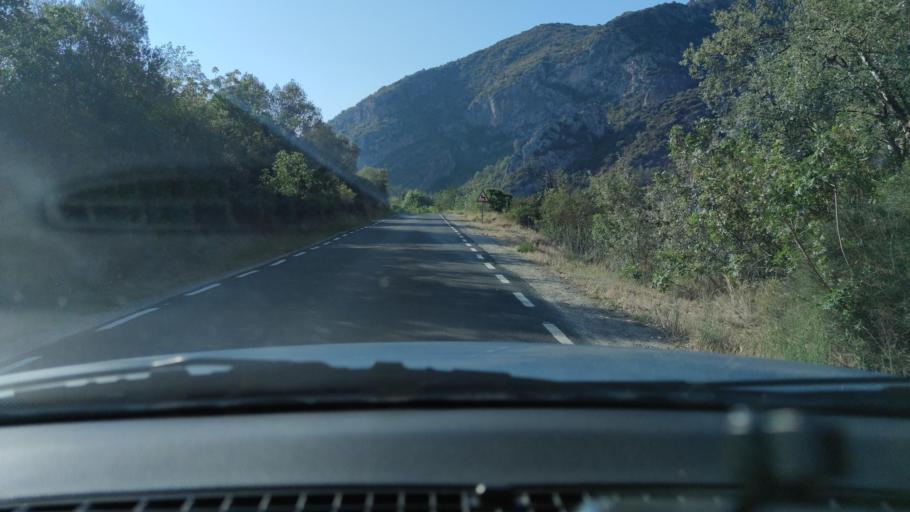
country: ES
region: Catalonia
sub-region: Provincia de Lleida
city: Camarasa
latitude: 41.8740
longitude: 0.8502
